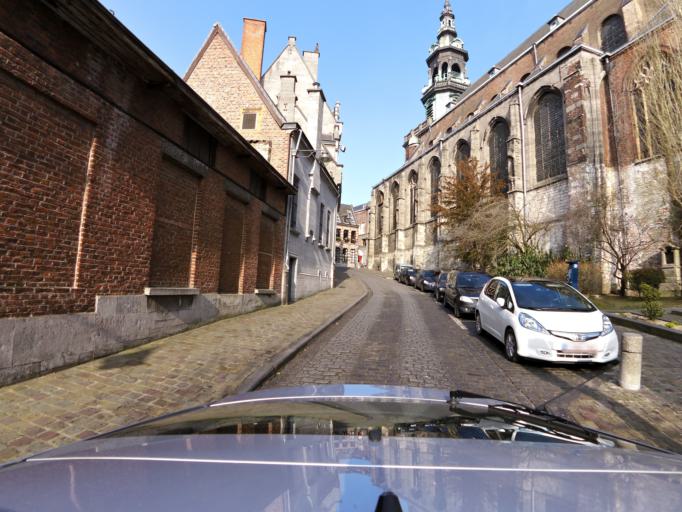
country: BE
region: Wallonia
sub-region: Province du Hainaut
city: Mons
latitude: 50.4552
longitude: 3.9542
